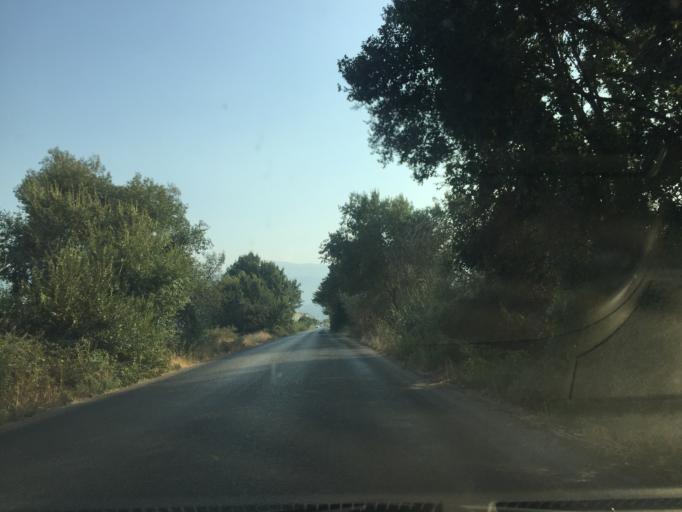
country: TR
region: Manisa
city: Salihli
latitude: 38.5035
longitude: 28.1868
